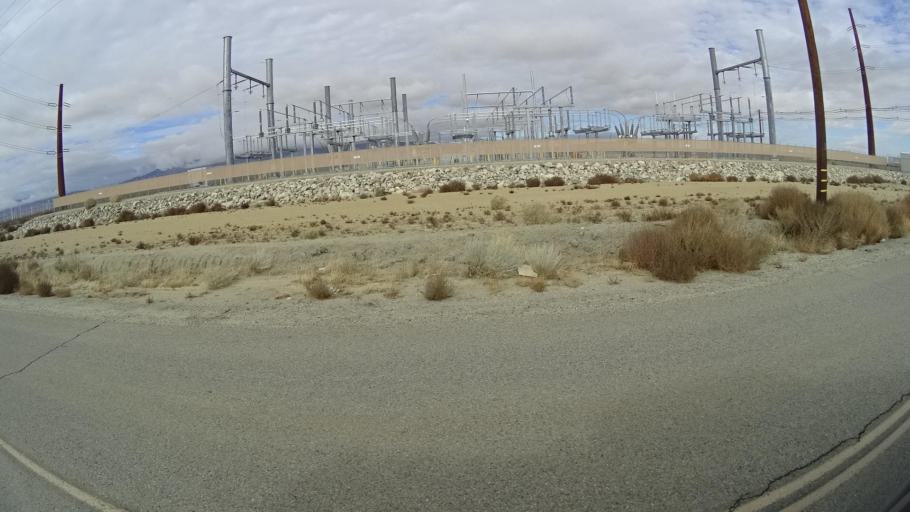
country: US
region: California
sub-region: Kern County
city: Rosamond
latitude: 34.8630
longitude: -118.3786
